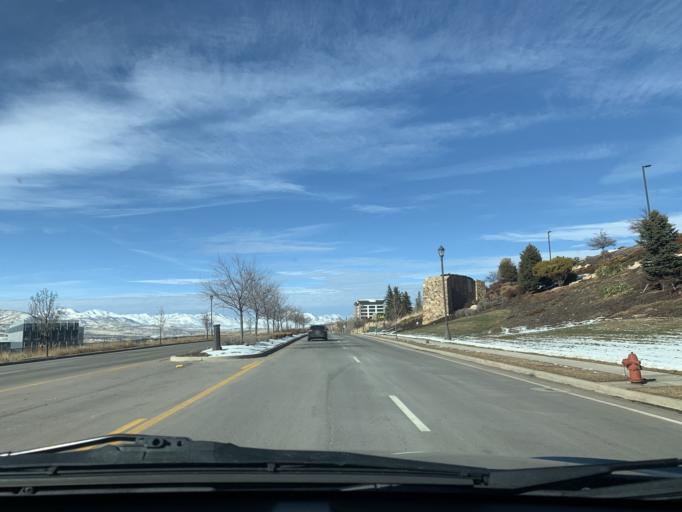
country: US
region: Utah
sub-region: Utah County
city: Lehi
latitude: 40.4341
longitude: -111.8871
